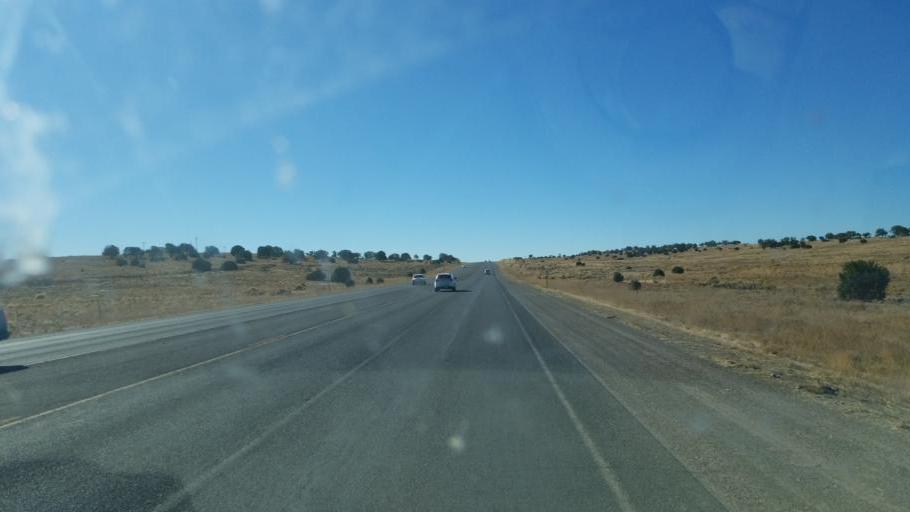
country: US
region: Arizona
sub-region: Apache County
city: Window Rock
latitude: 35.7066
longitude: -109.0631
